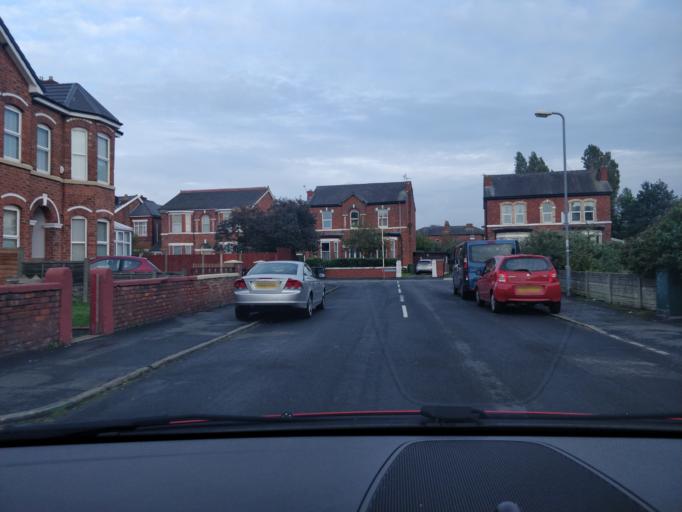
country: GB
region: England
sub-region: Sefton
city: Southport
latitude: 53.6415
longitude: -2.9942
